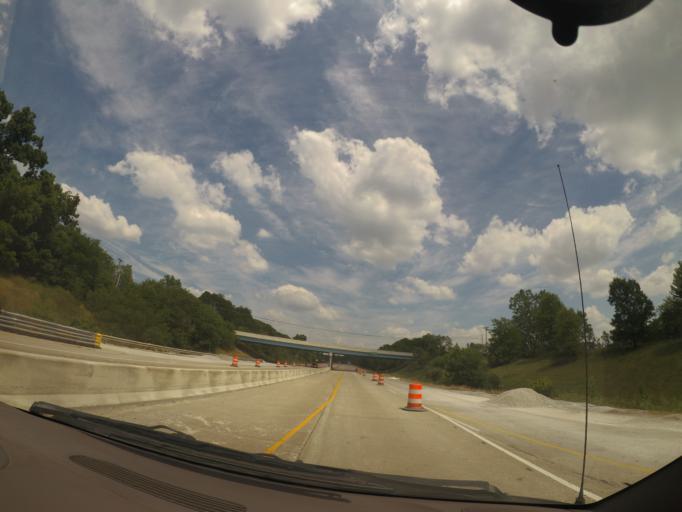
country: US
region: Indiana
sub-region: Elkhart County
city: Dunlap
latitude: 41.6572
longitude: -85.9159
